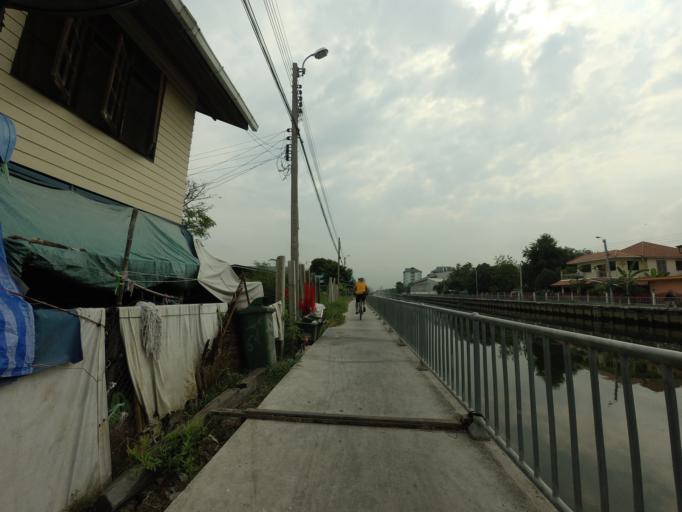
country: TH
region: Bangkok
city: Suan Luang
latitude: 13.7240
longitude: 100.6741
